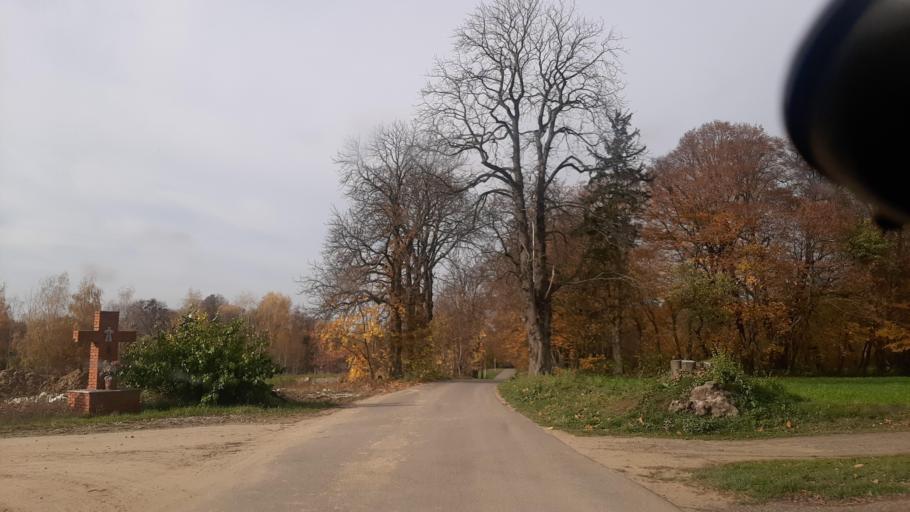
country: PL
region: Lublin Voivodeship
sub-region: Powiat lubelski
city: Jastkow
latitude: 51.3396
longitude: 22.4183
